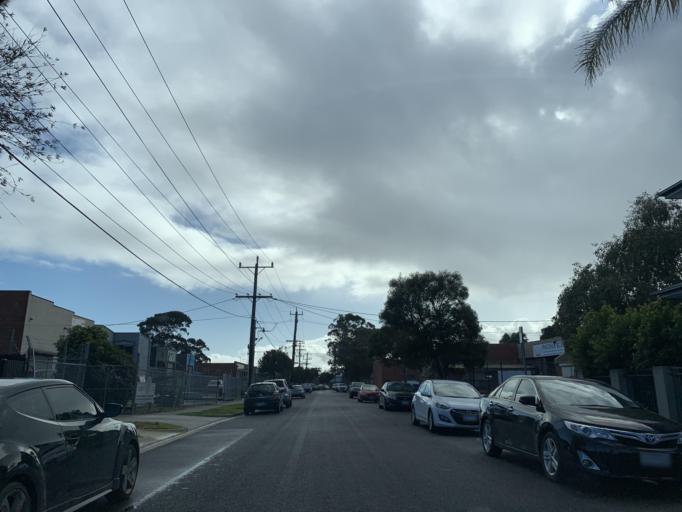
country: AU
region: Victoria
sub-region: Frankston
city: Seaford
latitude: -38.1165
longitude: 145.1320
